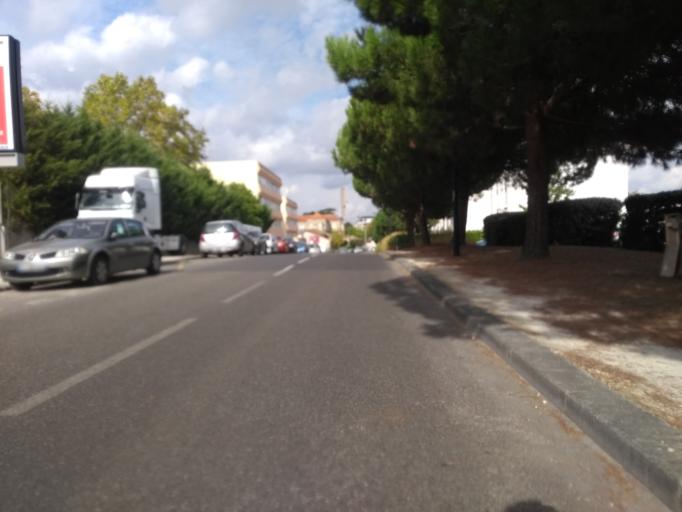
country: FR
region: Aquitaine
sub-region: Departement de la Gironde
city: Talence
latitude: 44.8233
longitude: -0.6108
